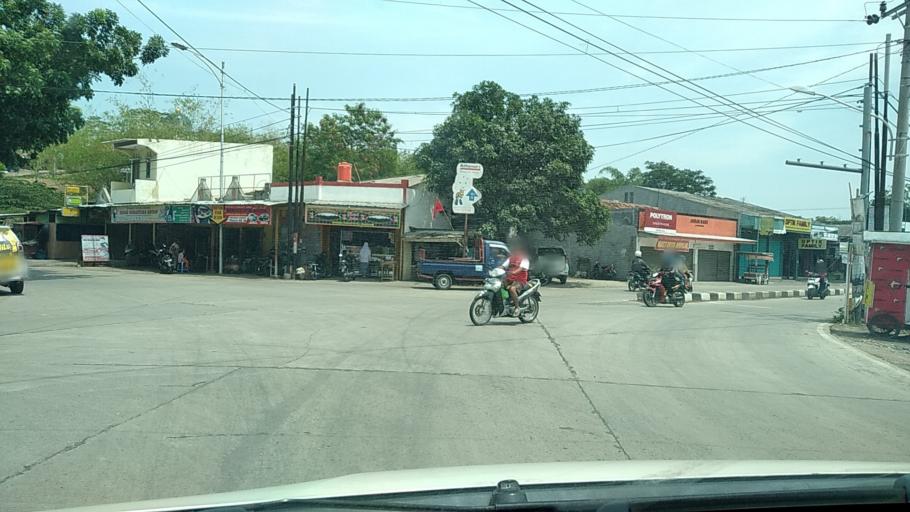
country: ID
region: Central Java
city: Mranggen
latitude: -7.0579
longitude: 110.4711
